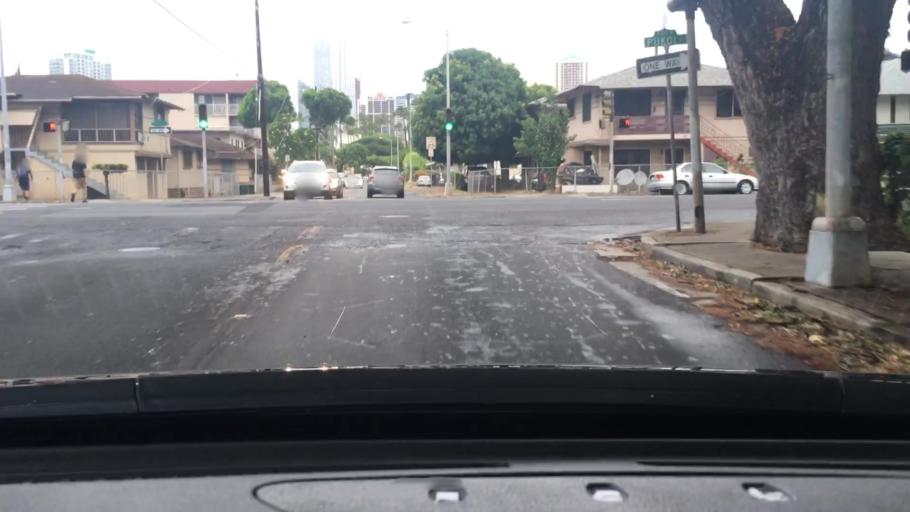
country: US
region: Hawaii
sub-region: Honolulu County
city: Honolulu
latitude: 21.2976
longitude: -157.8449
